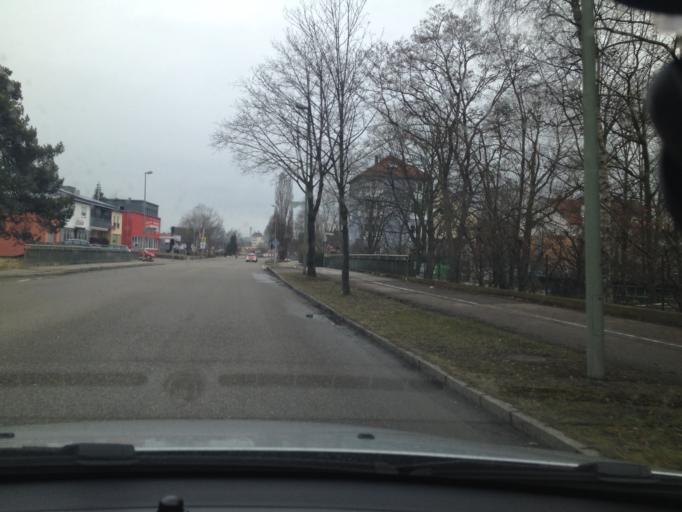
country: DE
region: Bavaria
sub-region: Swabia
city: Burgau
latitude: 48.4254
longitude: 10.4153
